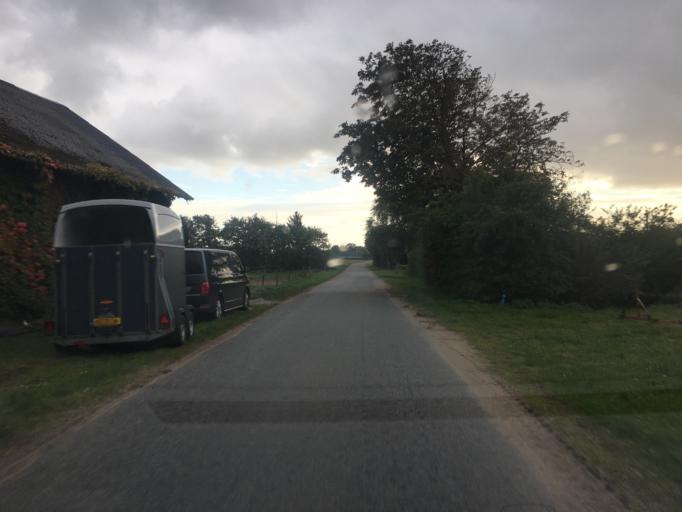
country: DK
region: South Denmark
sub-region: Tonder Kommune
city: Logumkloster
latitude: 55.0499
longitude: 8.9030
